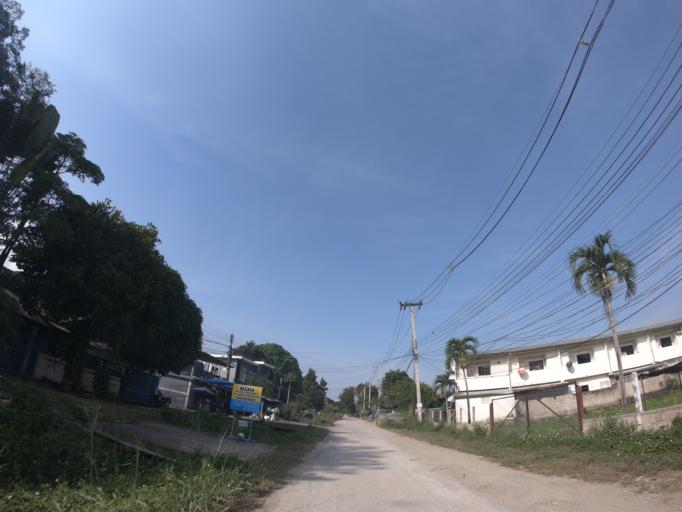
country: TH
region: Chiang Mai
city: Chiang Mai
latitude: 18.8242
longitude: 98.9932
